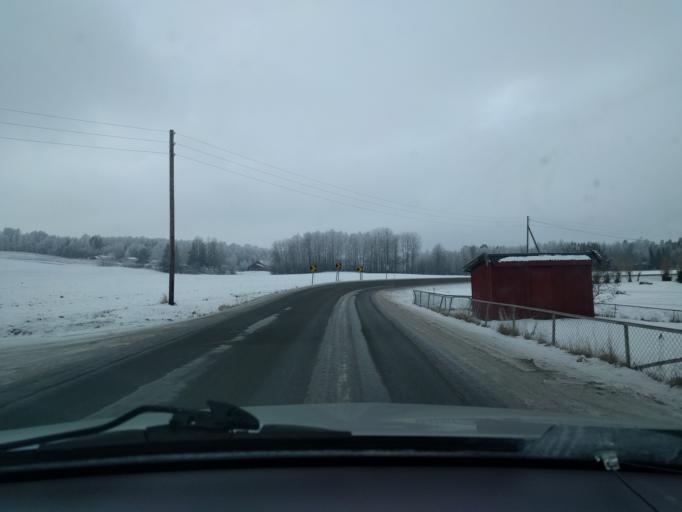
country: NO
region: Hedmark
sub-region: Hamar
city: Hamar
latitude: 60.7857
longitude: 11.1461
